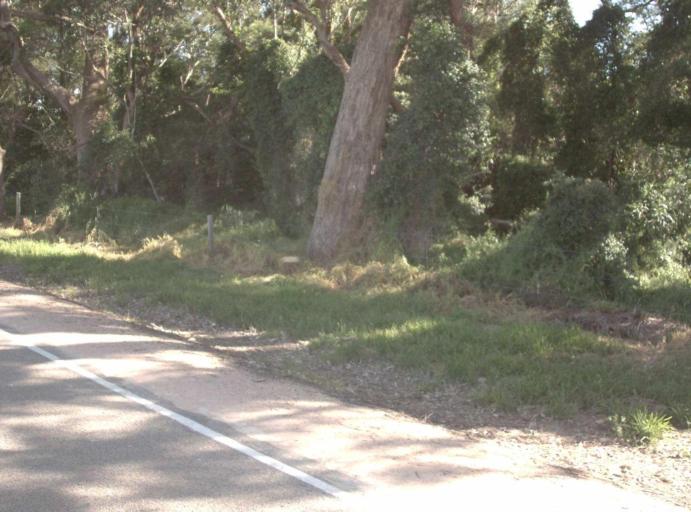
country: AU
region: Victoria
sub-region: East Gippsland
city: Lakes Entrance
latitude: -37.7387
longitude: 148.5055
